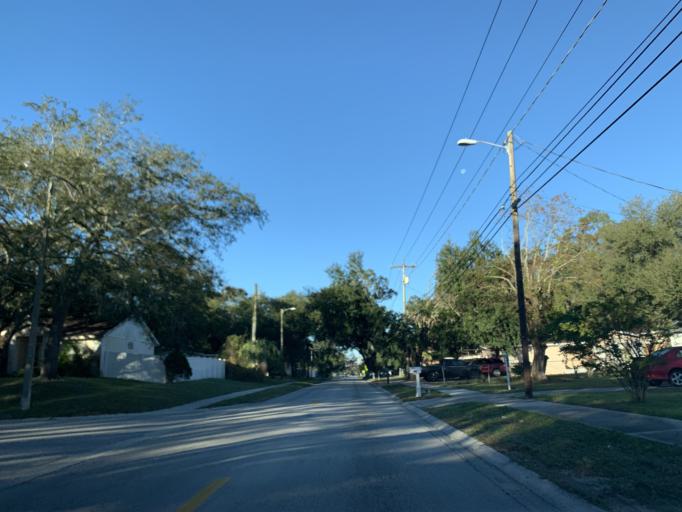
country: US
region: Florida
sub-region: Hillsborough County
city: University
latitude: 28.0436
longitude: -82.4320
